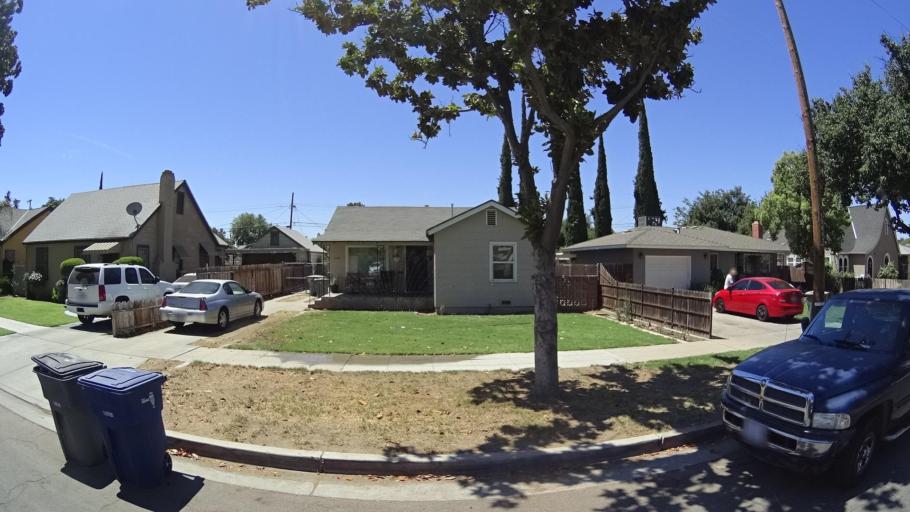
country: US
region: California
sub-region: Fresno County
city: Fresno
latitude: 36.7495
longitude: -119.7419
